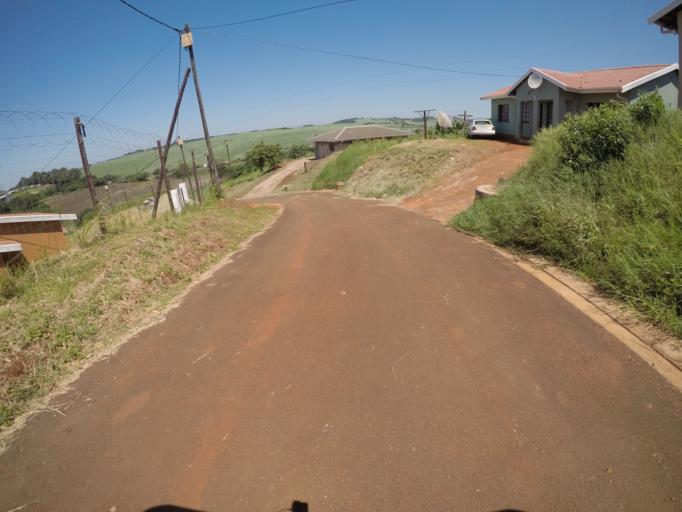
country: ZA
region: KwaZulu-Natal
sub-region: uThungulu District Municipality
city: Empangeni
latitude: -28.7751
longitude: 31.8825
